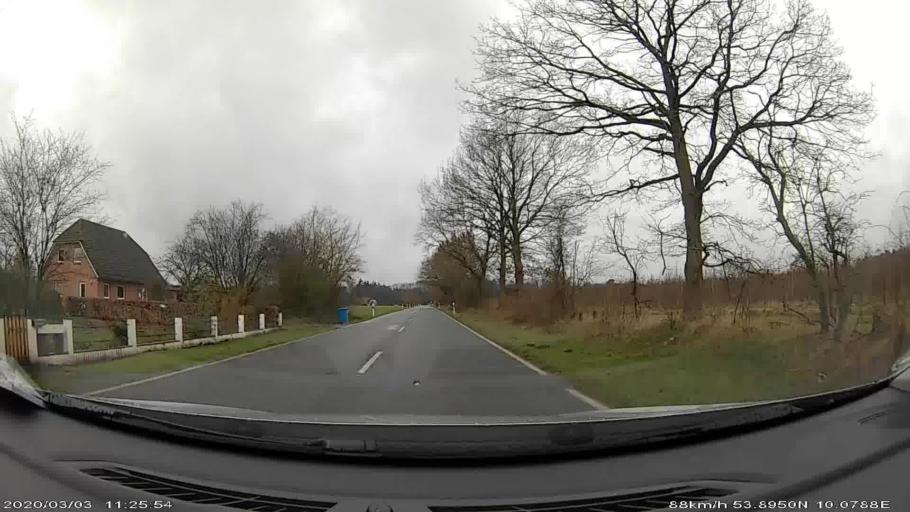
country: DE
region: Schleswig-Holstein
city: Hartenholm
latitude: 53.8971
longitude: 10.0746
